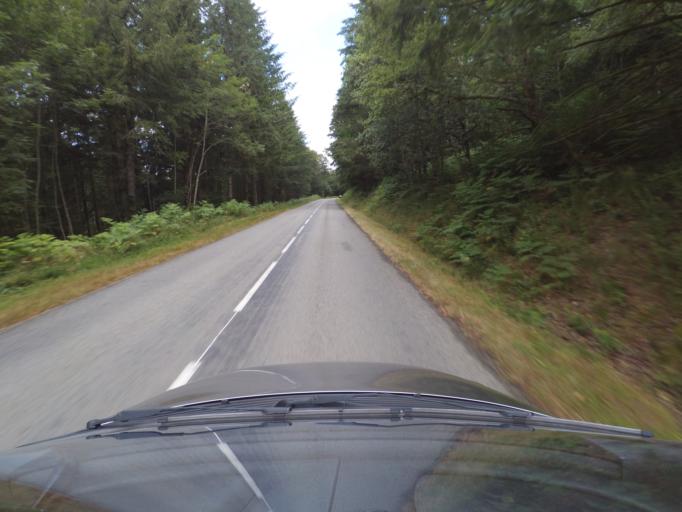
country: FR
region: Limousin
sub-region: Departement de la Creuse
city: Bourganeuf
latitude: 45.9018
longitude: 1.8593
